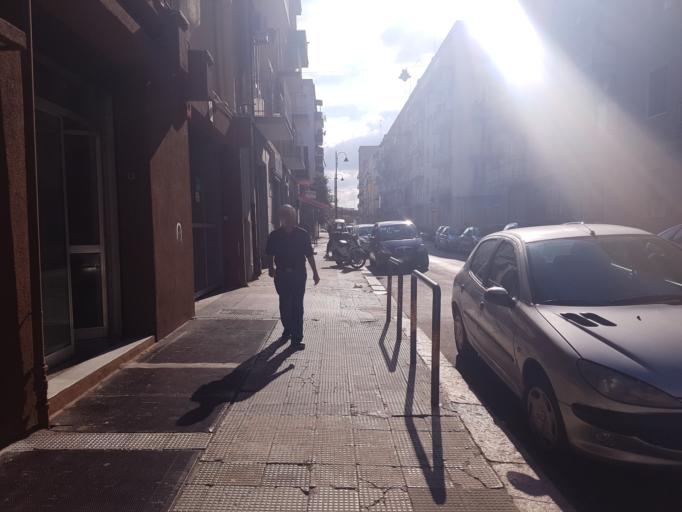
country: IT
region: Apulia
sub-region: Provincia di Bari
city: Bari
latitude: 41.1201
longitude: 16.8528
